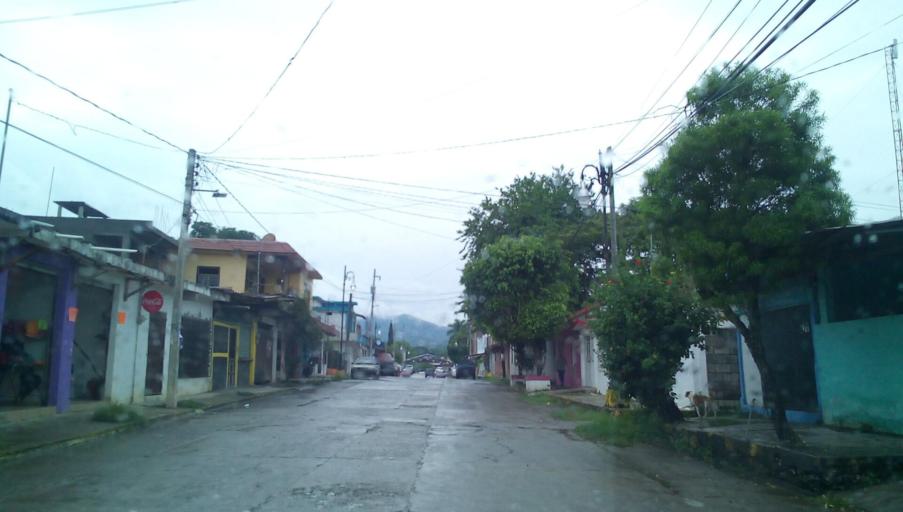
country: MX
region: Veracruz
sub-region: Chalma
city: San Pedro Coyutla
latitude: 21.2075
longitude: -98.3959
